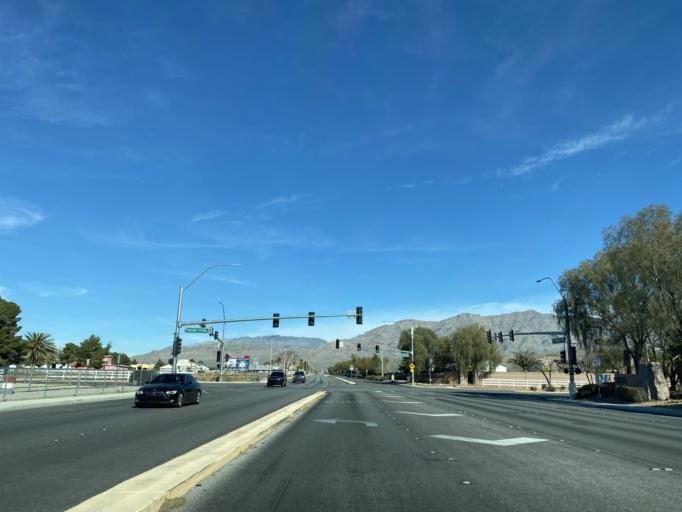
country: US
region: Nevada
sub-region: Clark County
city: North Las Vegas
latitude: 36.3043
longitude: -115.2240
